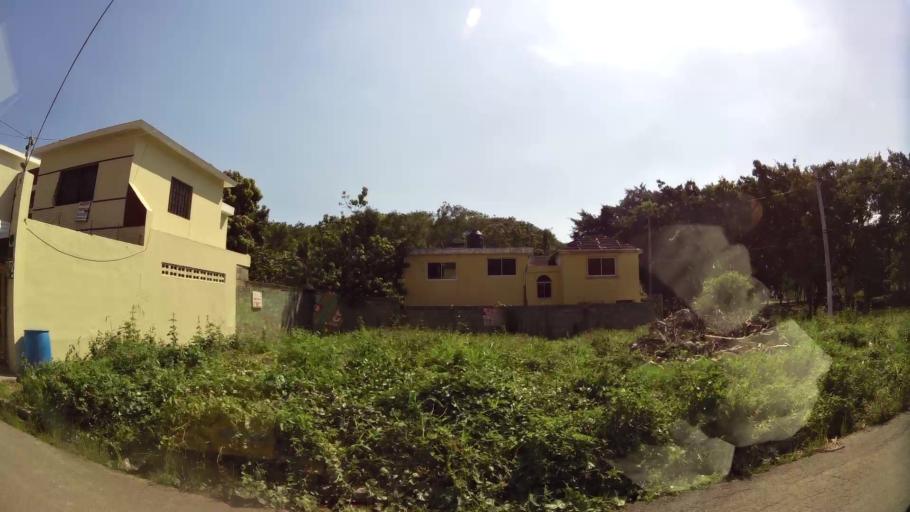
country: DO
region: Santo Domingo
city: Santo Domingo Oeste
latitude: 18.4751
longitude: -70.0057
